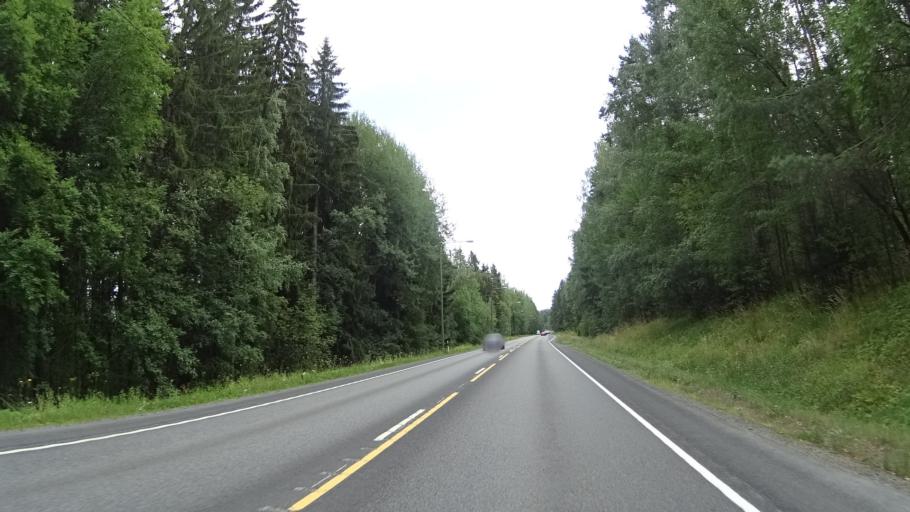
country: FI
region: Pirkanmaa
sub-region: Tampere
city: Kangasala
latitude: 61.4277
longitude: 24.1329
